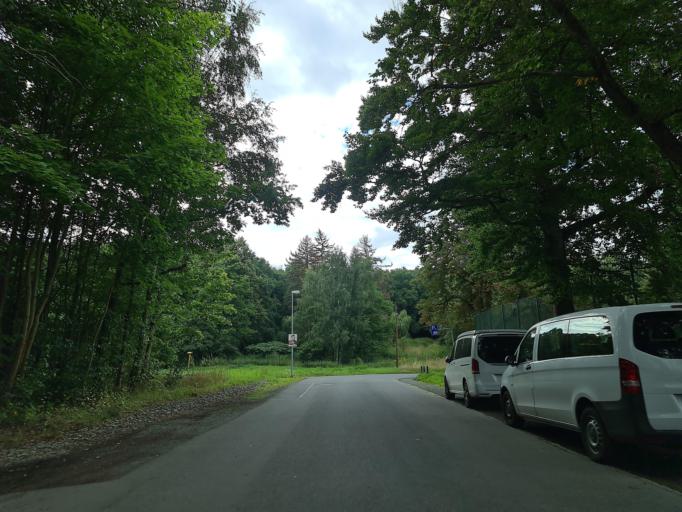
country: DE
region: Saxony
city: Plauen
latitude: 50.5230
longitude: 12.1227
